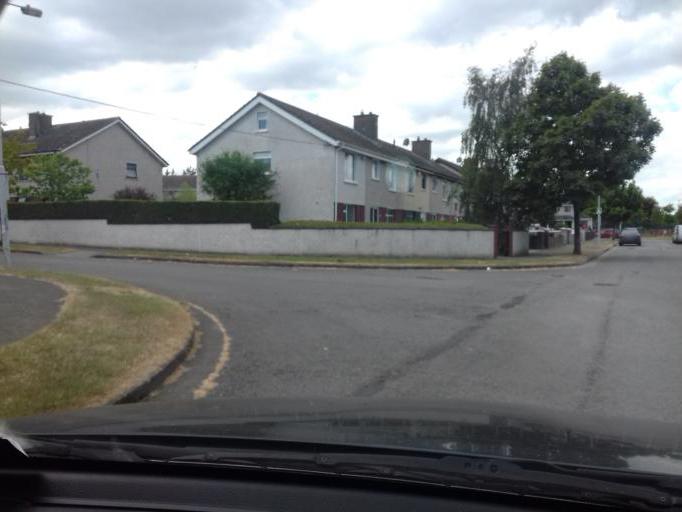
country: IE
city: Bonnybrook
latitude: 53.4060
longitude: -6.2139
